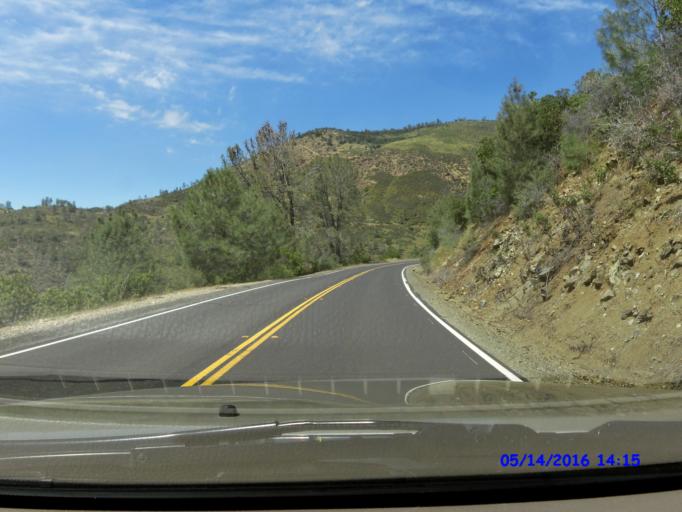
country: US
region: California
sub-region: Mariposa County
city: Mariposa
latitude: 37.6550
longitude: -120.1495
